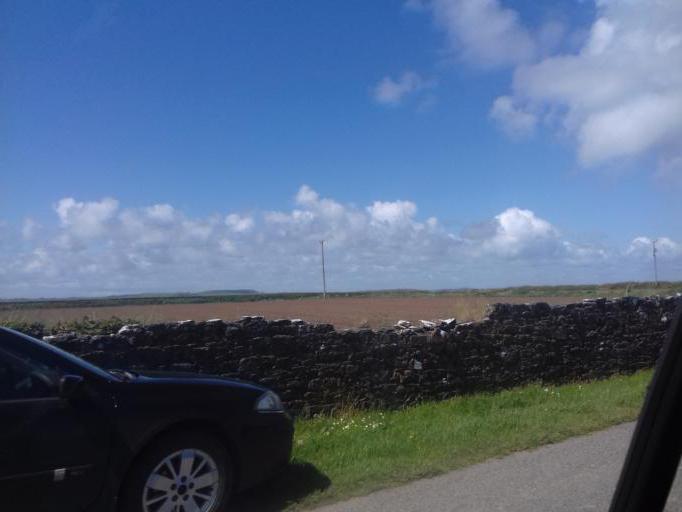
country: IE
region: Munster
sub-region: Waterford
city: Dunmore East
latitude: 52.1361
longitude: -6.9167
